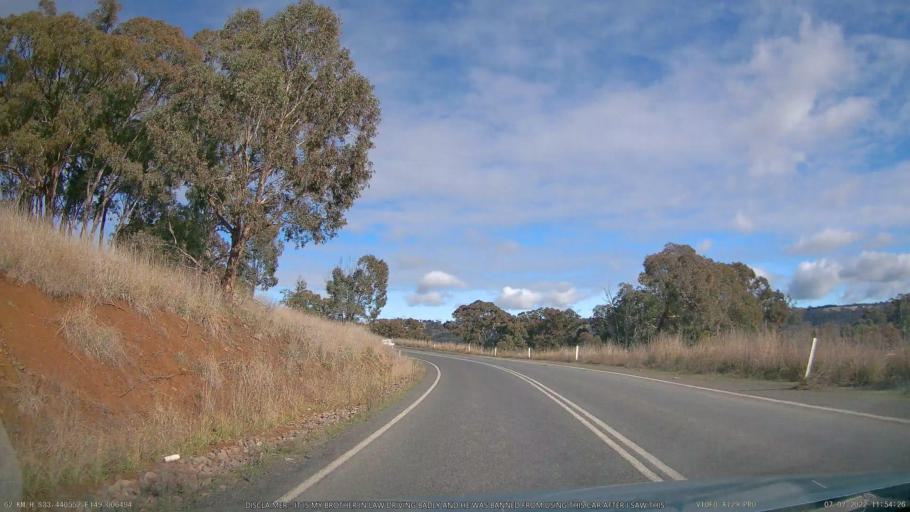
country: AU
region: New South Wales
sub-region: Blayney
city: Millthorpe
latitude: -33.4407
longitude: 149.0060
